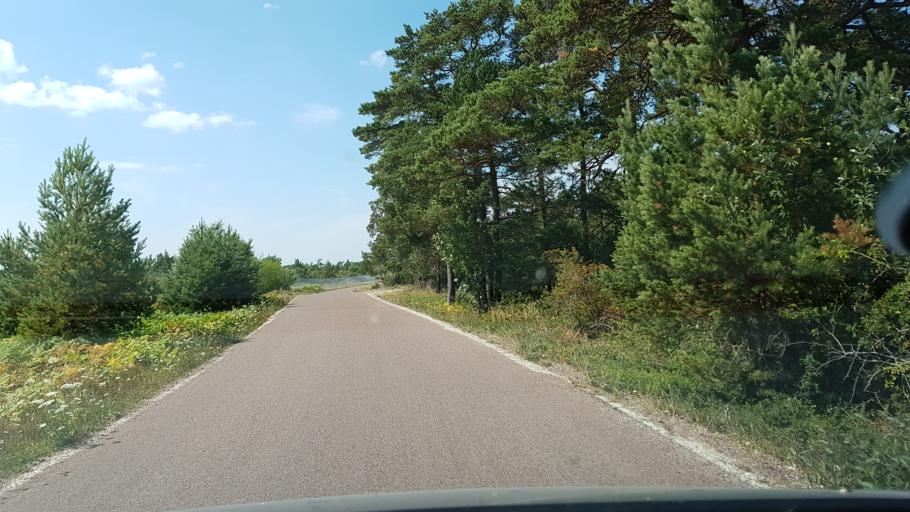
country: SE
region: Gotland
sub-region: Gotland
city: Visby
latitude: 57.6840
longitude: 18.3634
